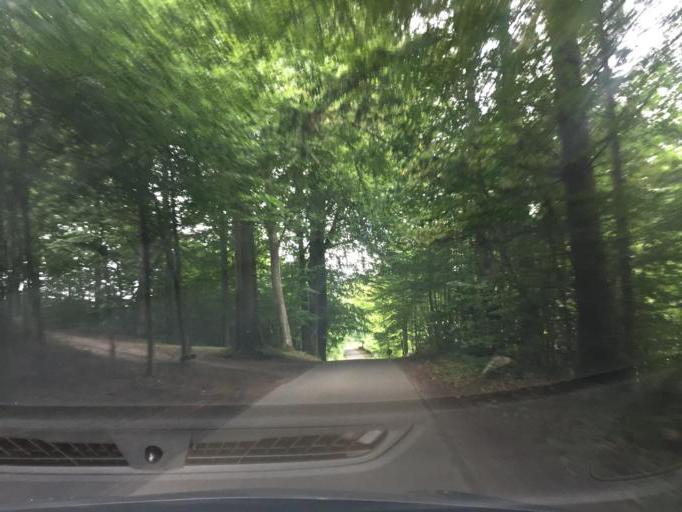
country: DK
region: South Denmark
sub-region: Assens Kommune
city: Tommerup Stationsby
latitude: 55.3655
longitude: 10.2176
